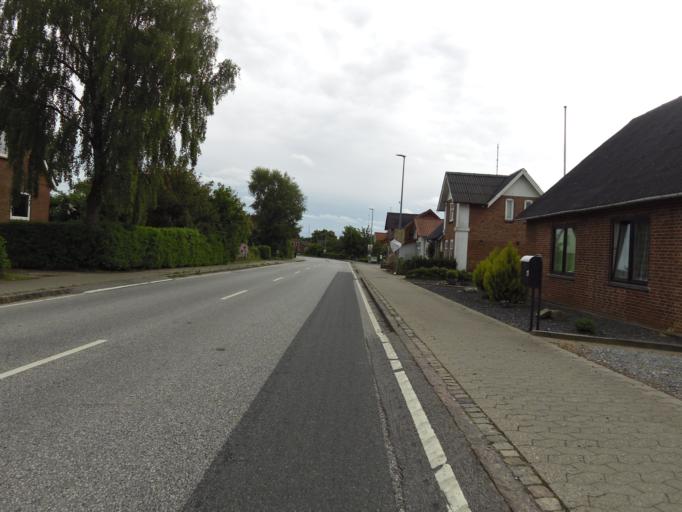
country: DK
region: South Denmark
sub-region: Vejen Kommune
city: Rodding
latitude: 55.3322
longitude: 9.0567
